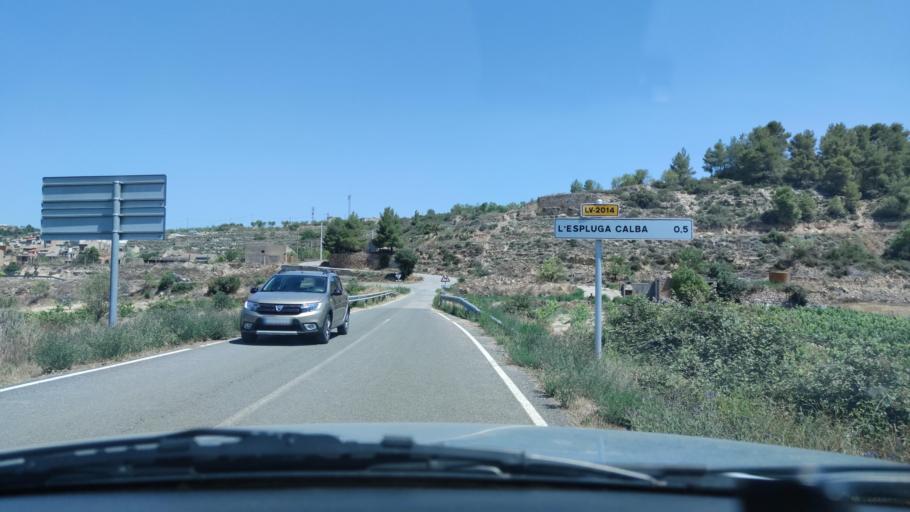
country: ES
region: Catalonia
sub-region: Provincia de Lleida
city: Fulleda
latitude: 41.4901
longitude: 1.0089
